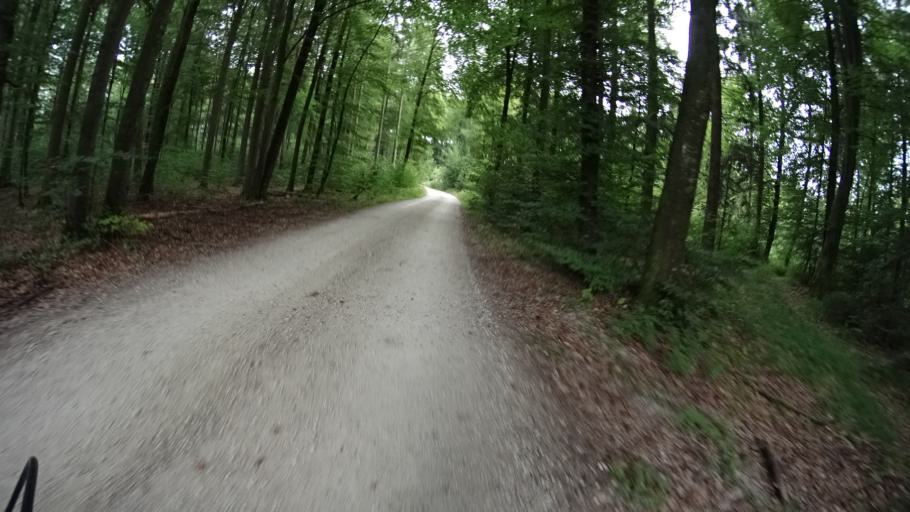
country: DE
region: Bavaria
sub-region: Upper Bavaria
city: Hitzhofen
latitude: 48.8846
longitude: 11.3282
